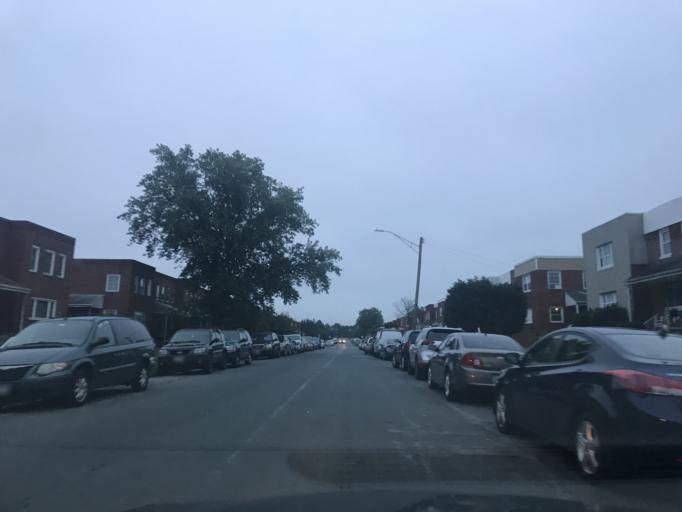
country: US
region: Maryland
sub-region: Baltimore County
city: Dundalk
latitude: 39.2711
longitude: -76.4899
